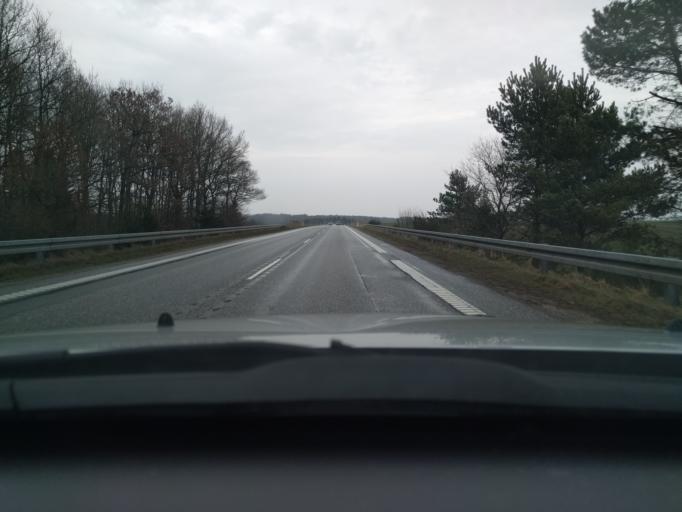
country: DK
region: Central Jutland
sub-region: Viborg Kommune
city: Viborg
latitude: 56.3924
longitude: 9.3229
